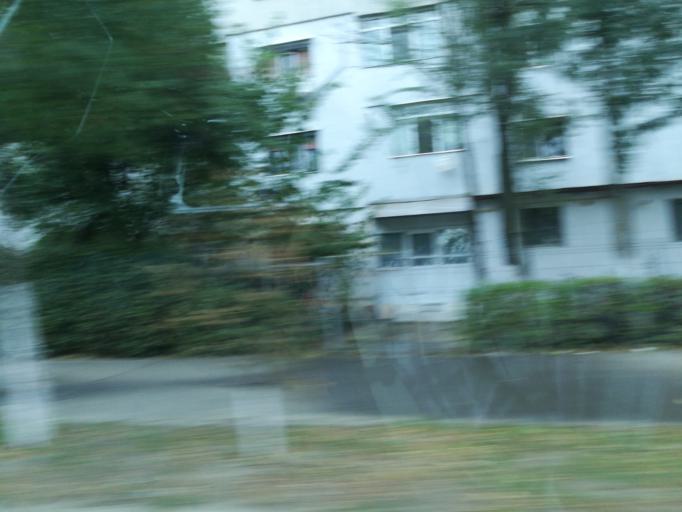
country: RO
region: Galati
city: Galati
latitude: 45.4551
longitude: 28.0150
